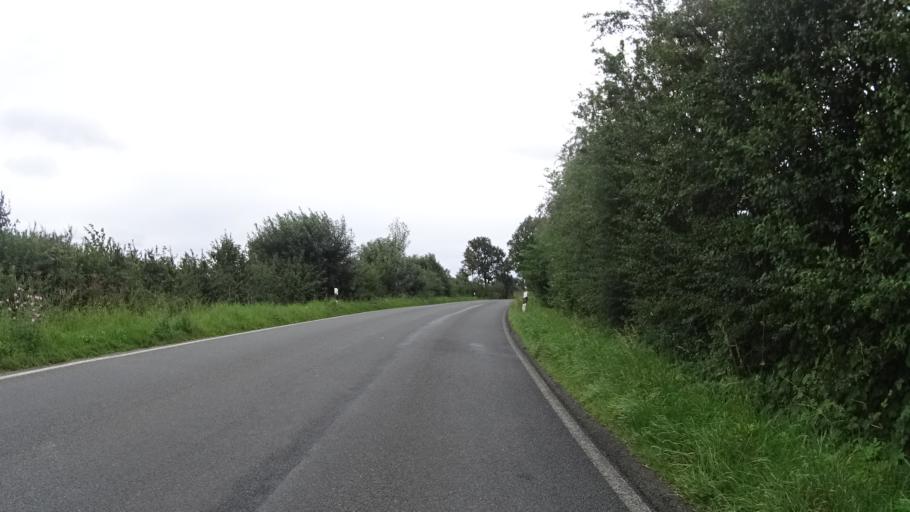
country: DE
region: Schleswig-Holstein
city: Klinkrade
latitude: 53.7118
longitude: 10.5606
